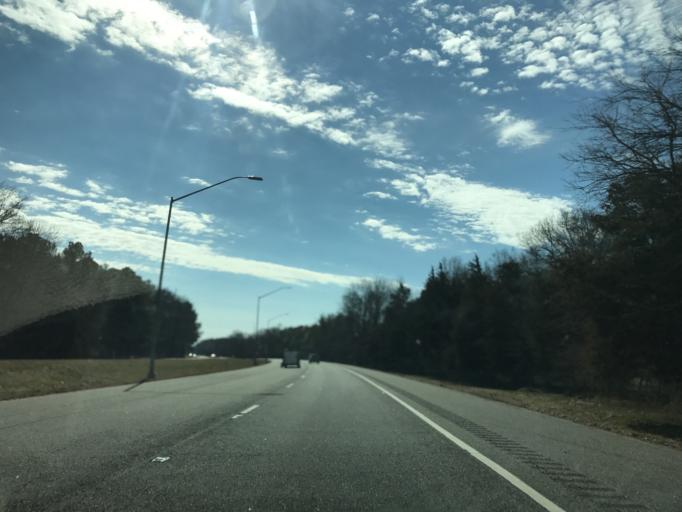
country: US
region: Maryland
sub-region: Queen Anne's County
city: Kingstown
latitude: 39.2395
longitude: -75.8754
